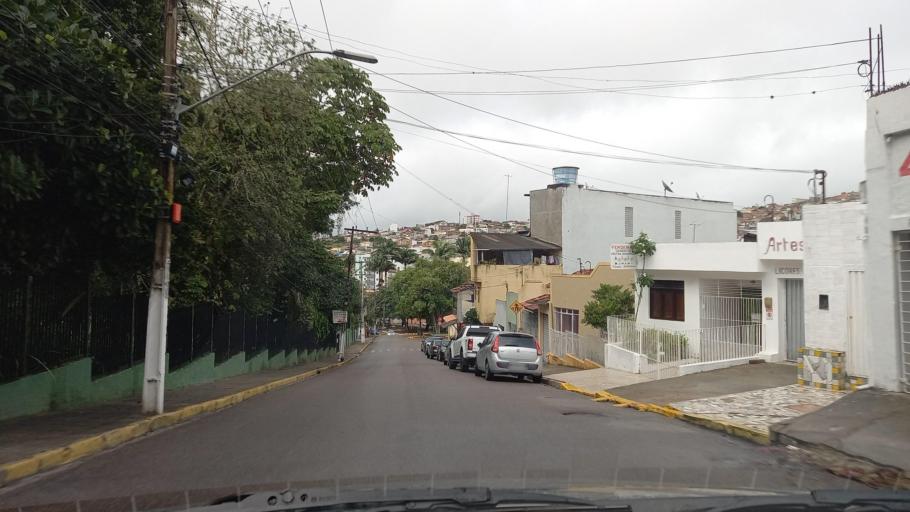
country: BR
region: Pernambuco
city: Garanhuns
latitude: -8.8928
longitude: -36.4917
